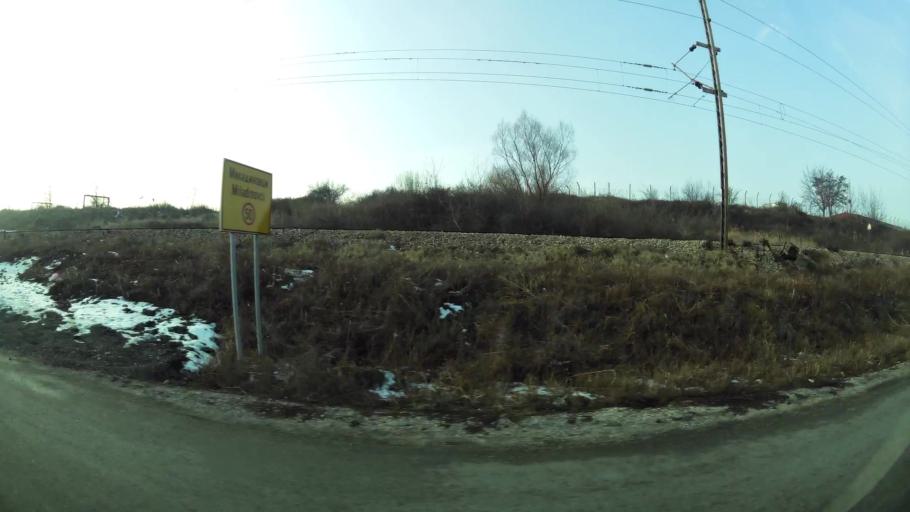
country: MK
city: Miladinovci
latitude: 41.9914
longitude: 21.6541
